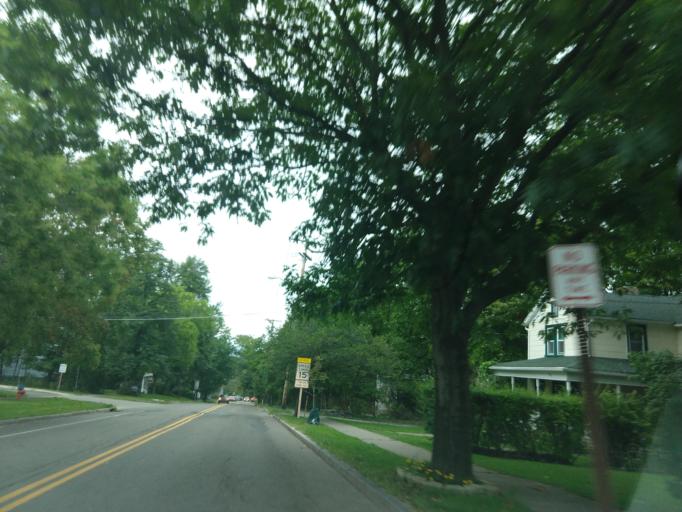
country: US
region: New York
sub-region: Tompkins County
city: South Hill
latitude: 42.4338
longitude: -76.4917
